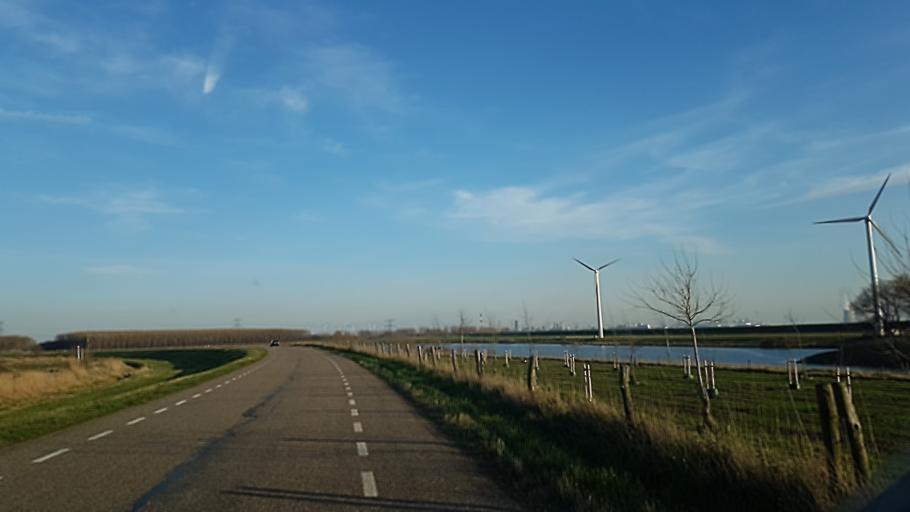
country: NL
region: North Brabant
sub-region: Gemeente Woensdrecht
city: Woensdrecht
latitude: 51.4029
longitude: 4.2183
